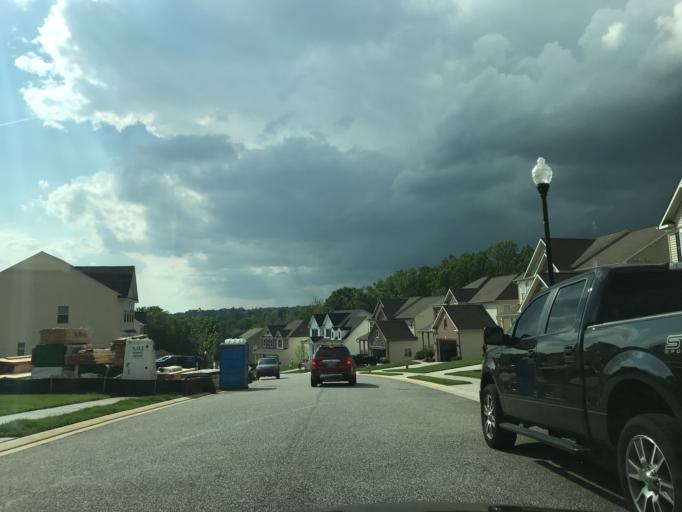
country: US
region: Maryland
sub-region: Harford County
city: Bel Air North
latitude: 39.5523
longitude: -76.3806
